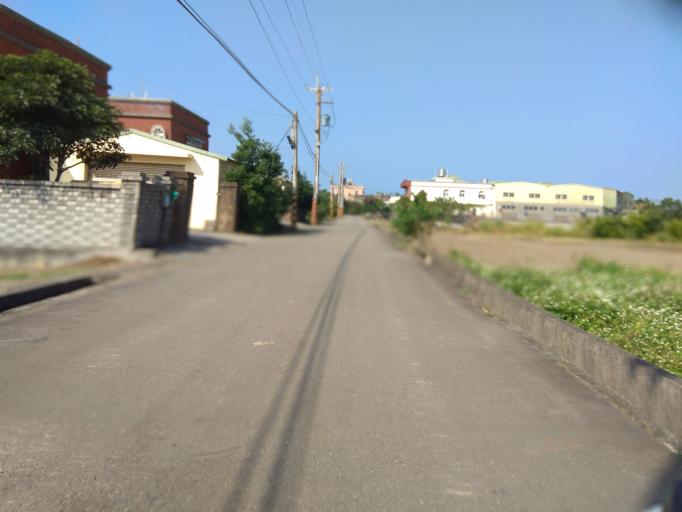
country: TW
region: Taiwan
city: Taoyuan City
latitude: 25.0492
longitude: 121.2156
